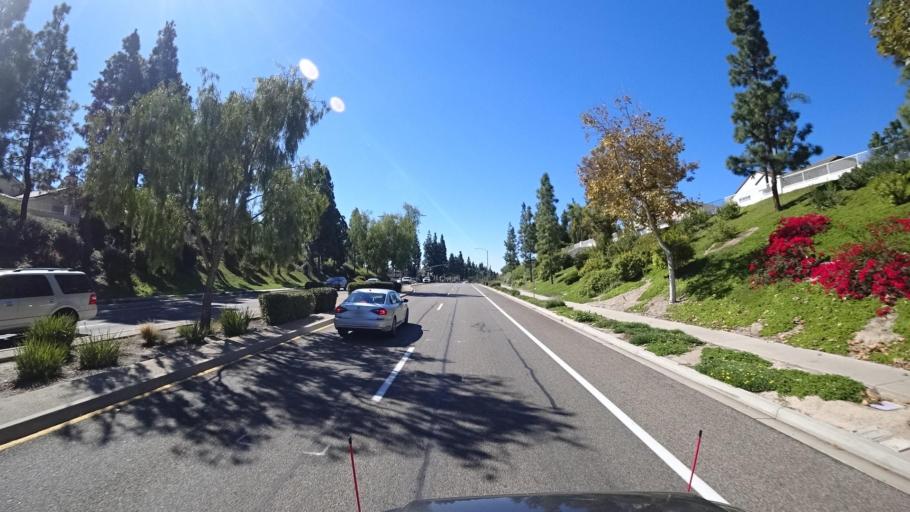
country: US
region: California
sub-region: San Diego County
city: Bonita
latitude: 32.6562
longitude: -116.9796
